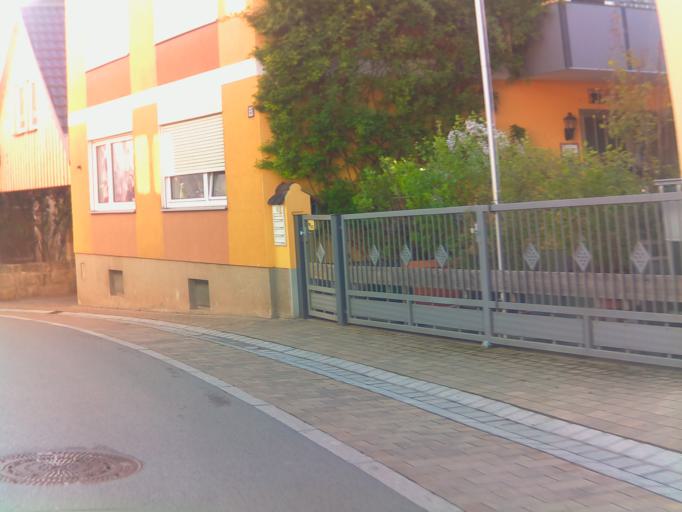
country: DE
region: Bavaria
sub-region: Regierungsbezirk Unterfranken
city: Ramsthal
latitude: 50.1517
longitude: 10.0676
